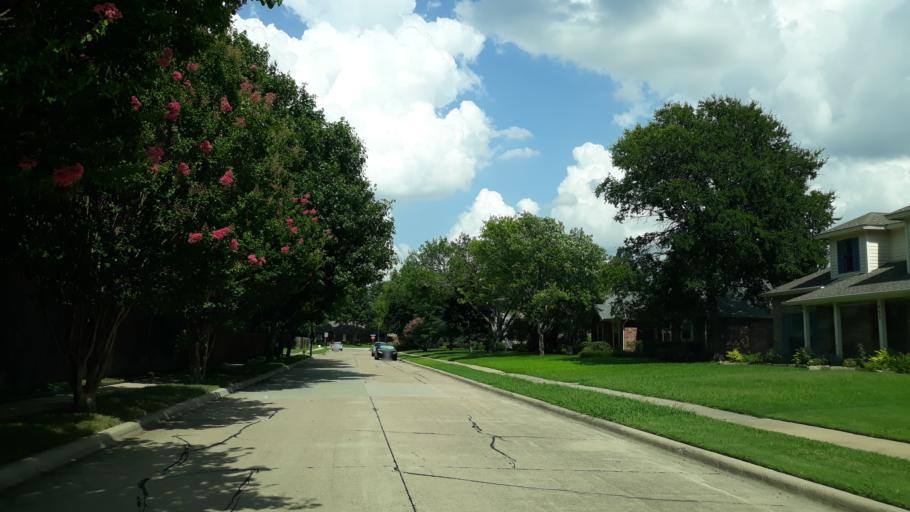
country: US
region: Texas
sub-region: Dallas County
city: Coppell
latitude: 32.9647
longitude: -97.0025
